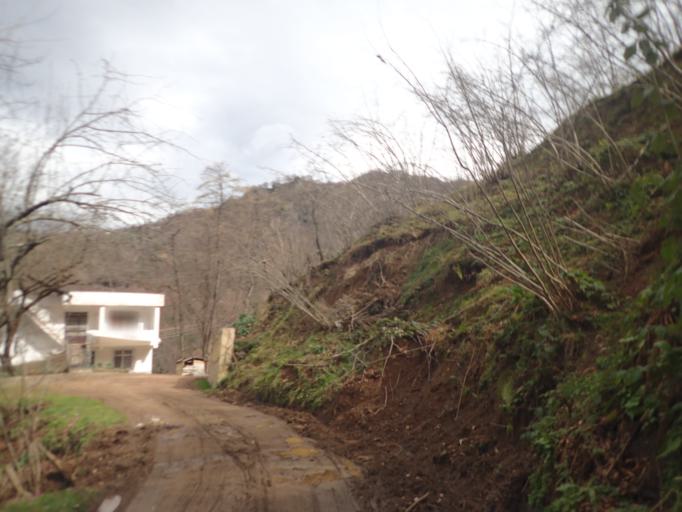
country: TR
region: Ordu
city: Camas
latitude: 40.8950
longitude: 37.5791
